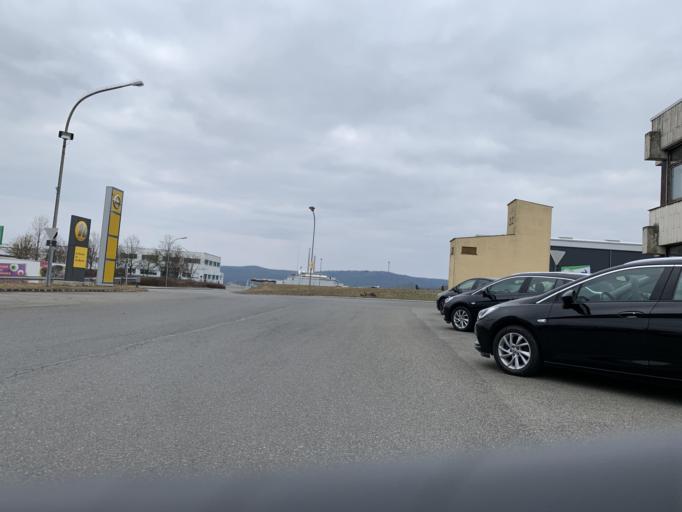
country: DE
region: Bavaria
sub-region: Upper Palatinate
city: Neunburg vorm Wald
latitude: 49.3379
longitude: 12.3957
